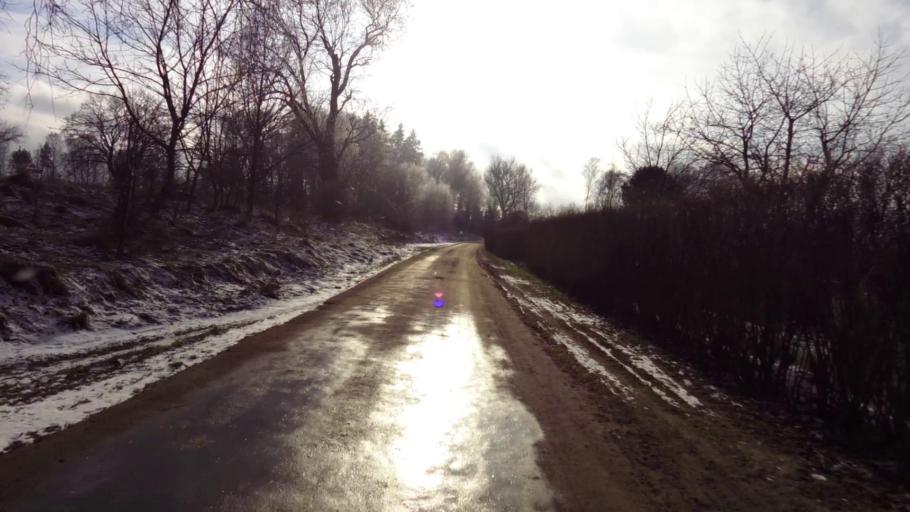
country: PL
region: West Pomeranian Voivodeship
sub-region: Powiat drawski
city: Zlocieniec
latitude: 53.5453
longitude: 16.0172
